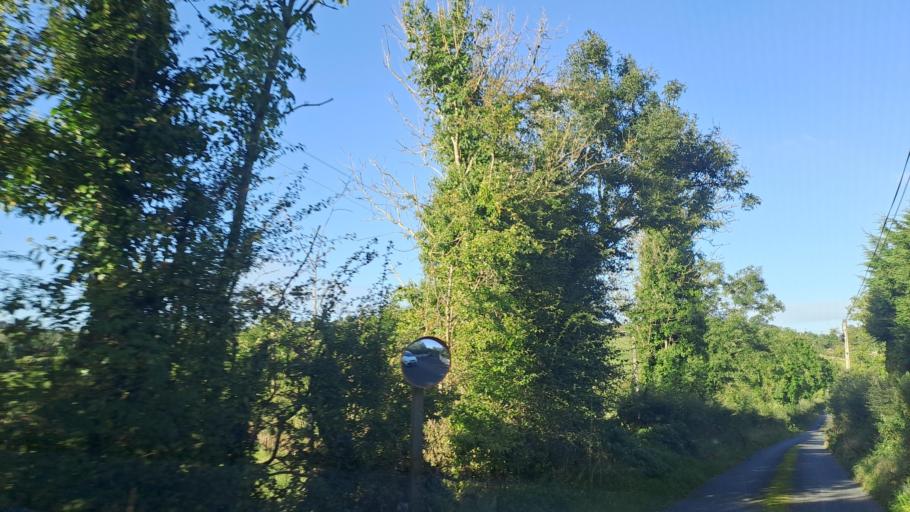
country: IE
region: Ulster
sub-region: An Cabhan
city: Kingscourt
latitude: 53.9886
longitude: -6.8629
